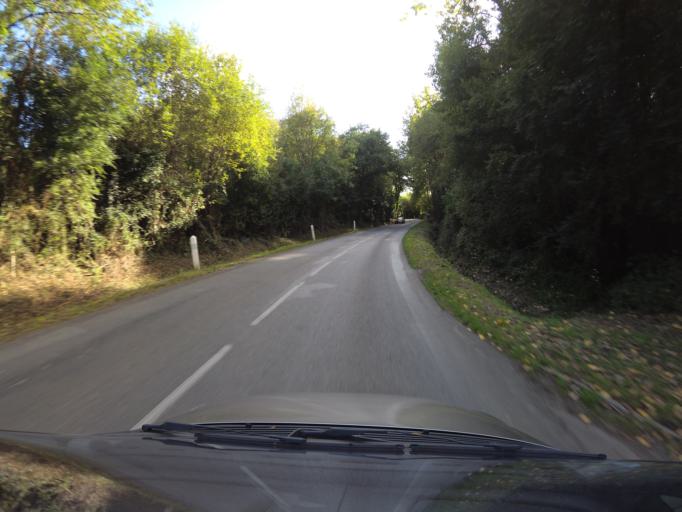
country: FR
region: Brittany
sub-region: Departement du Morbihan
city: Peillac
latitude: 47.7198
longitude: -2.2139
